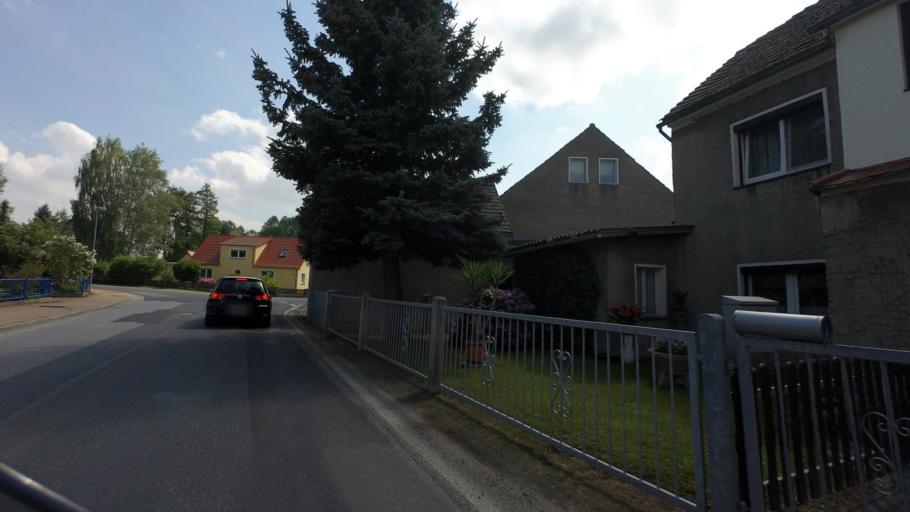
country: DE
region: Saxony
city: Weissenberg
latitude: 51.2589
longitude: 14.6460
